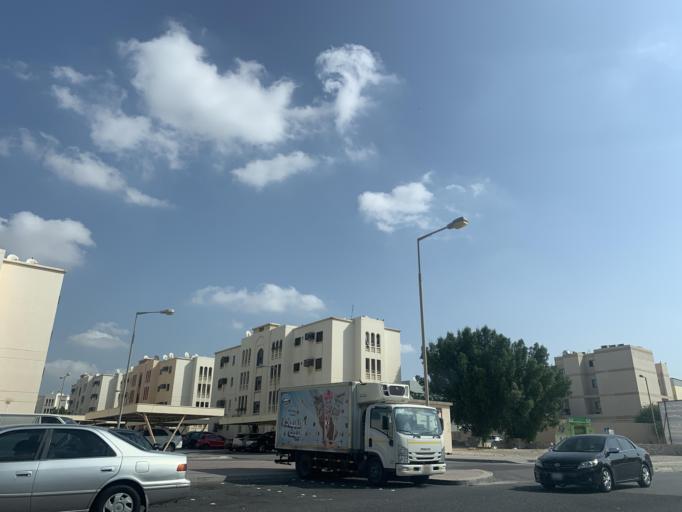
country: BH
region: Central Governorate
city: Madinat Hamad
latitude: 26.1326
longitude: 50.4995
